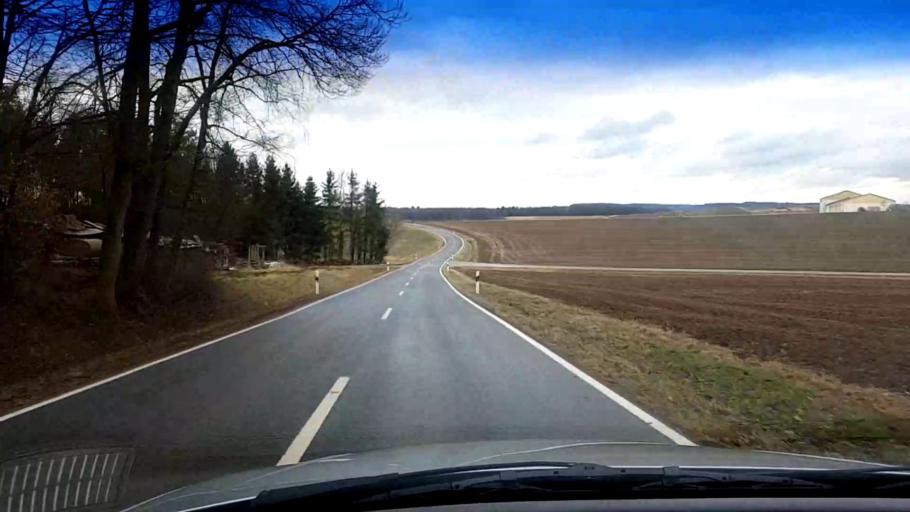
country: DE
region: Bavaria
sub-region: Upper Franconia
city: Zapfendorf
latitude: 50.0076
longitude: 10.9760
